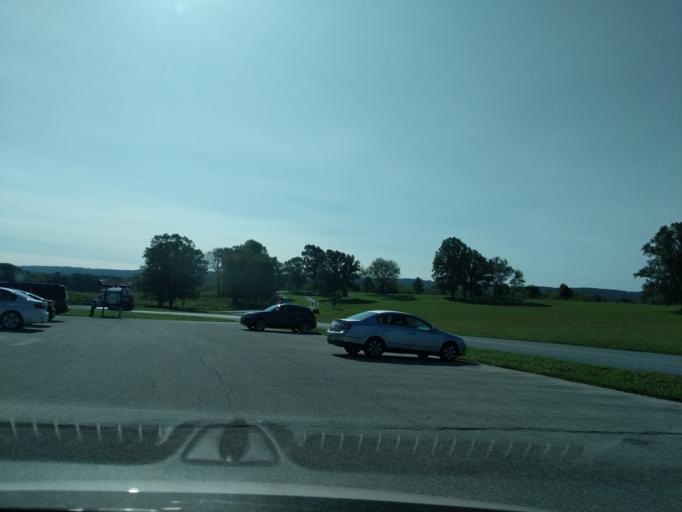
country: US
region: Pennsylvania
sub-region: Chester County
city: Chesterbrook
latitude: 40.0913
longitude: -75.4393
